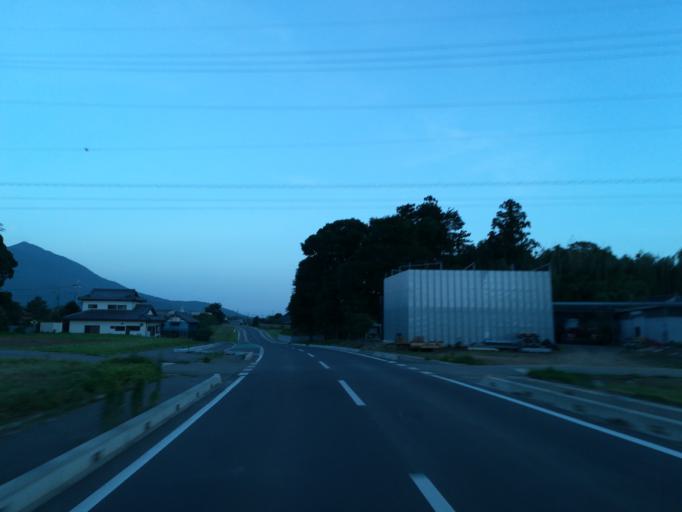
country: JP
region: Ibaraki
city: Makabe
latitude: 36.2749
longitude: 140.0552
